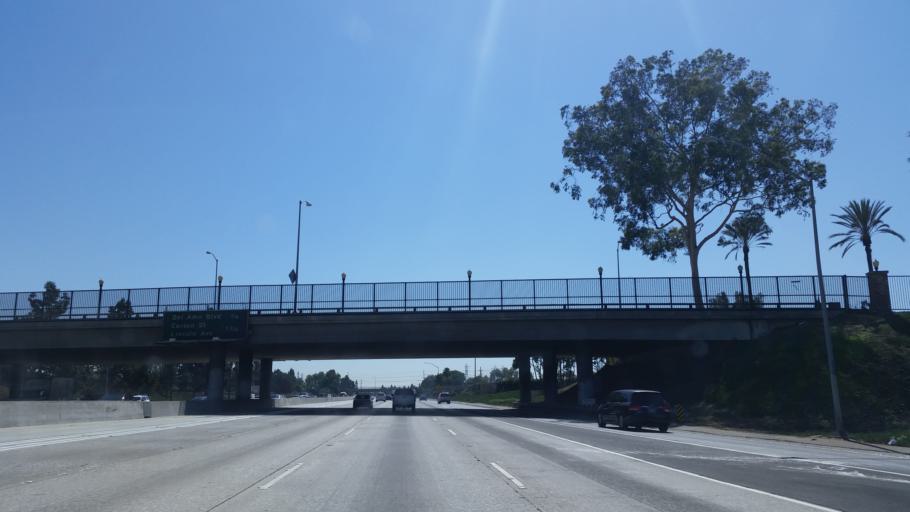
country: US
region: California
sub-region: Los Angeles County
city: Artesia
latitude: 33.8592
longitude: -118.0965
